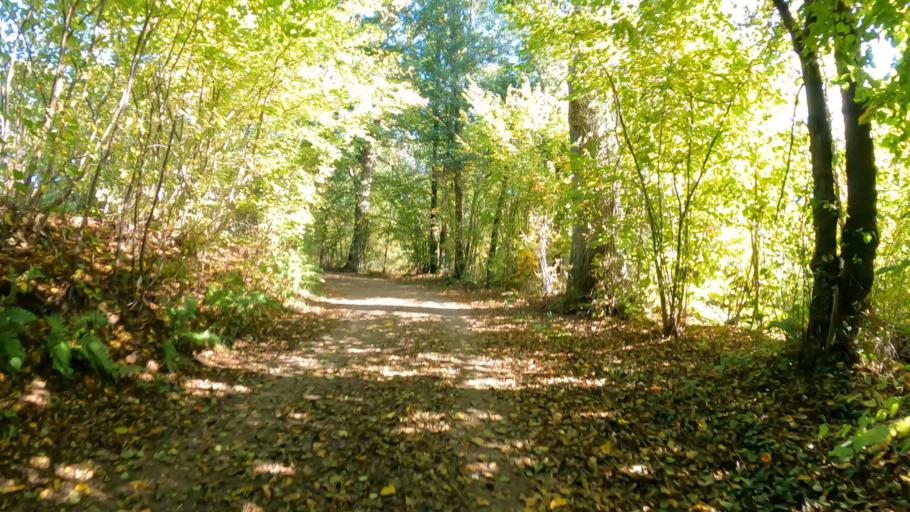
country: DE
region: Schleswig-Holstein
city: Ahrensburg
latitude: 53.6896
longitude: 10.2232
